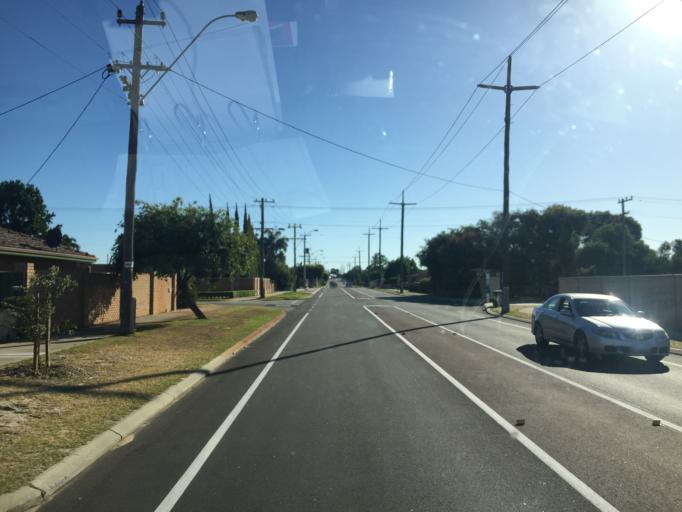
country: AU
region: Western Australia
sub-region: Belmont
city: Rivervale
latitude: -31.9637
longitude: 115.9252
